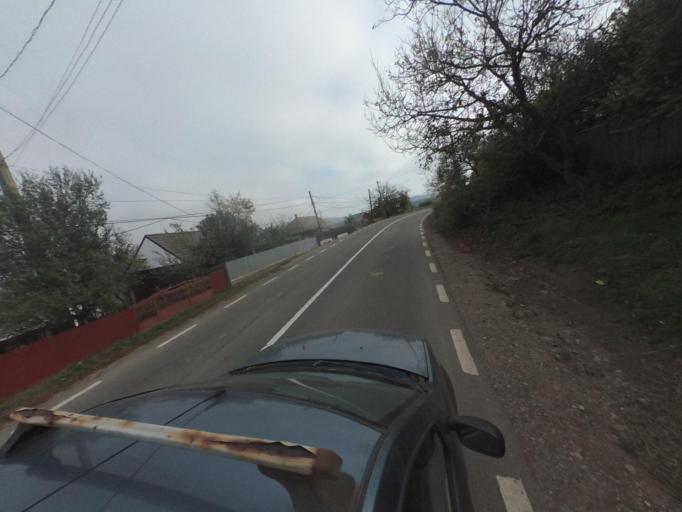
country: RO
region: Vaslui
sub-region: Comuna Bacesti
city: Bacesti
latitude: 46.8290
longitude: 27.2406
